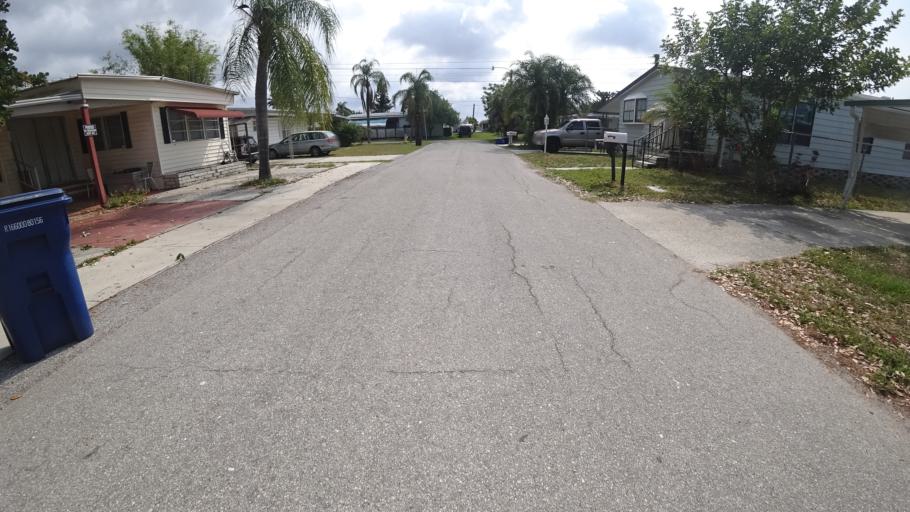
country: US
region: Florida
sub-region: Manatee County
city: South Bradenton
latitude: 27.4499
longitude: -82.5717
